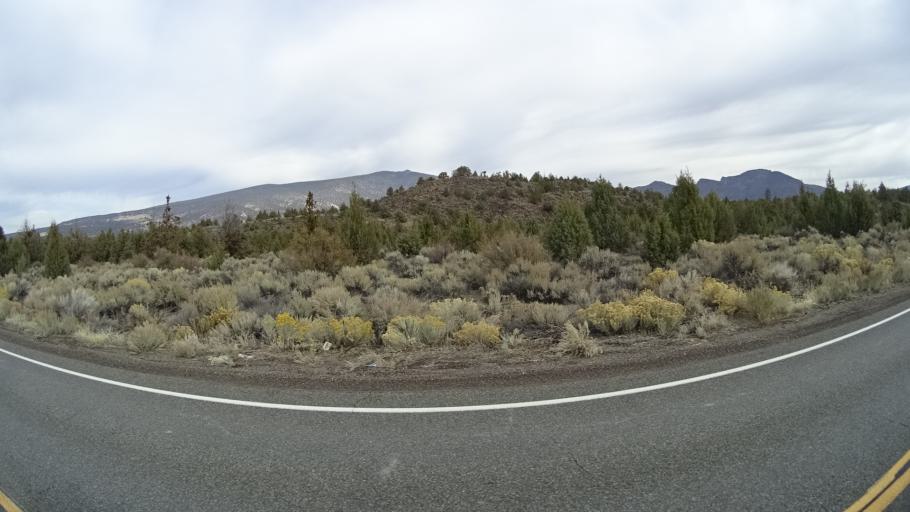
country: US
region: California
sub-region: Siskiyou County
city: Weed
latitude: 41.5763
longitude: -122.2830
